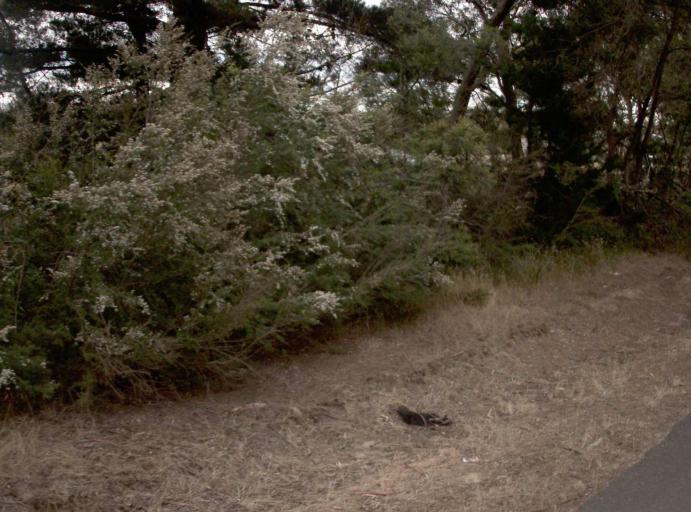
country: AU
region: Victoria
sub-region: Wellington
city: Sale
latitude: -38.2101
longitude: 147.0667
